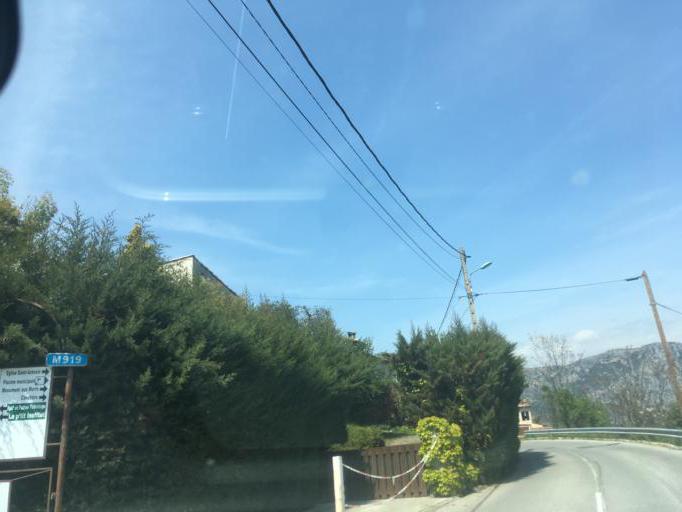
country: FR
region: Provence-Alpes-Cote d'Azur
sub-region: Departement des Alpes-Maritimes
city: Levens
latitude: 43.8627
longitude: 7.2259
